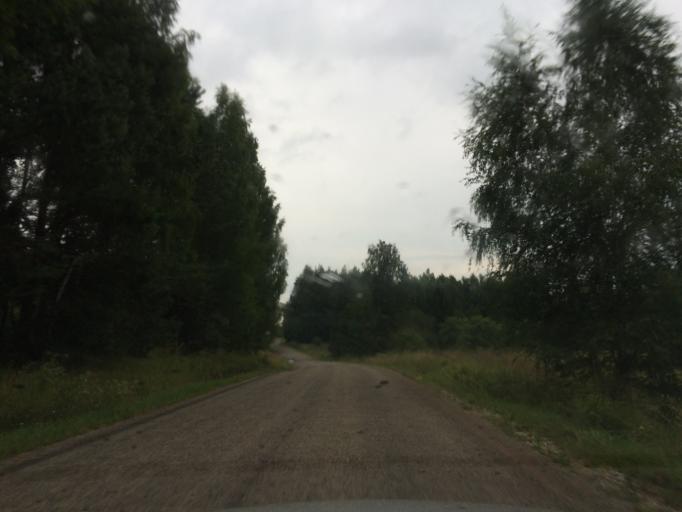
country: LV
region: Rezekne
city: Rezekne
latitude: 56.5682
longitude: 27.4619
